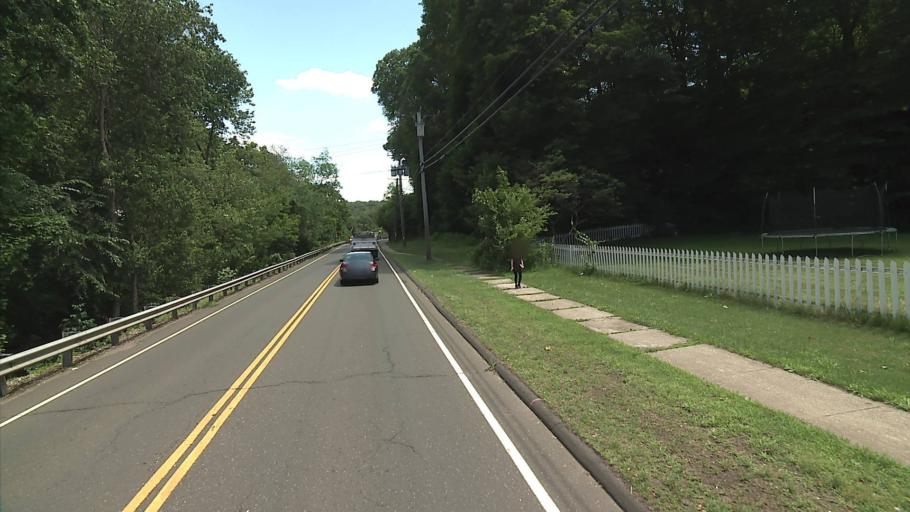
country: US
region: Connecticut
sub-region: New Haven County
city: Naugatuck
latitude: 41.5002
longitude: -73.0566
